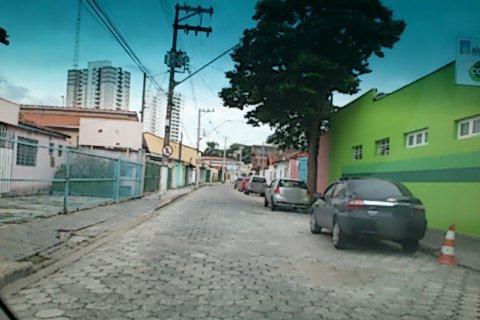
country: BR
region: Sao Paulo
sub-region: Jacarei
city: Jacarei
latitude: -23.2997
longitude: -45.9695
